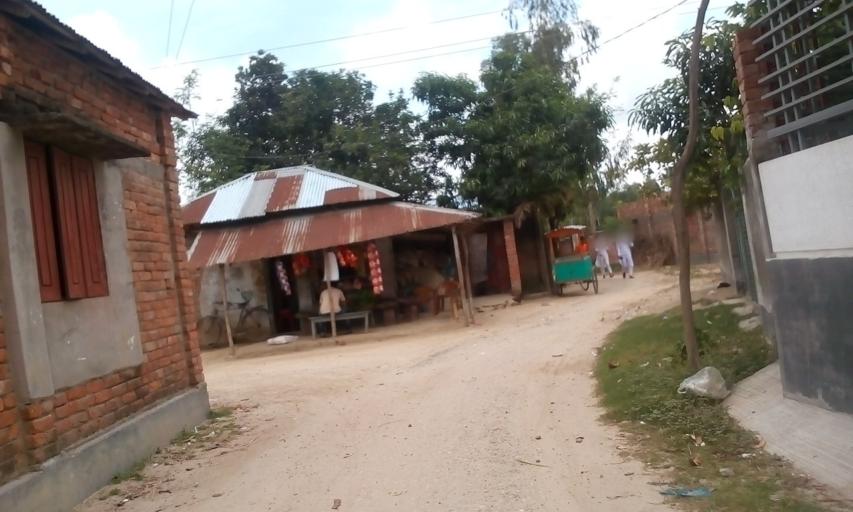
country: IN
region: West Bengal
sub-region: Dakshin Dinajpur
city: Balurghat
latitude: 25.3950
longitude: 88.9846
